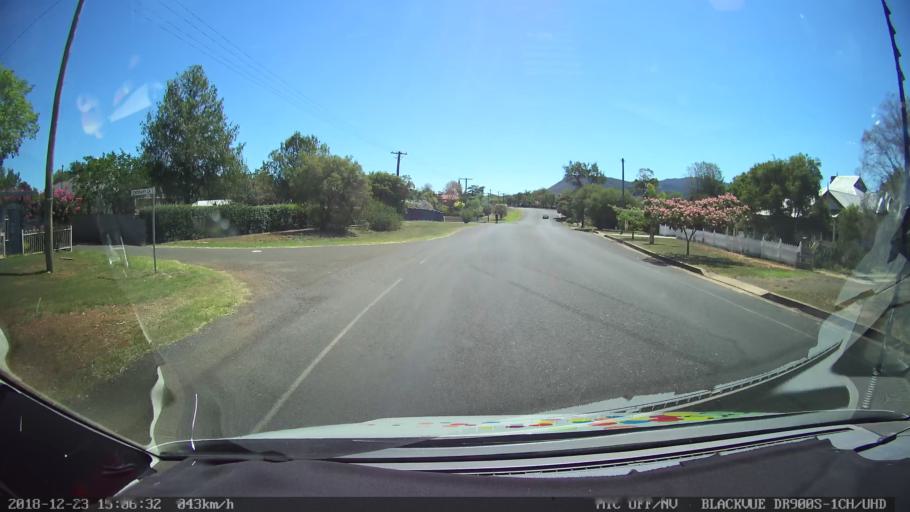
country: AU
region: New South Wales
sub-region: Tamworth Municipality
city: Manilla
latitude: -30.7456
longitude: 150.7278
